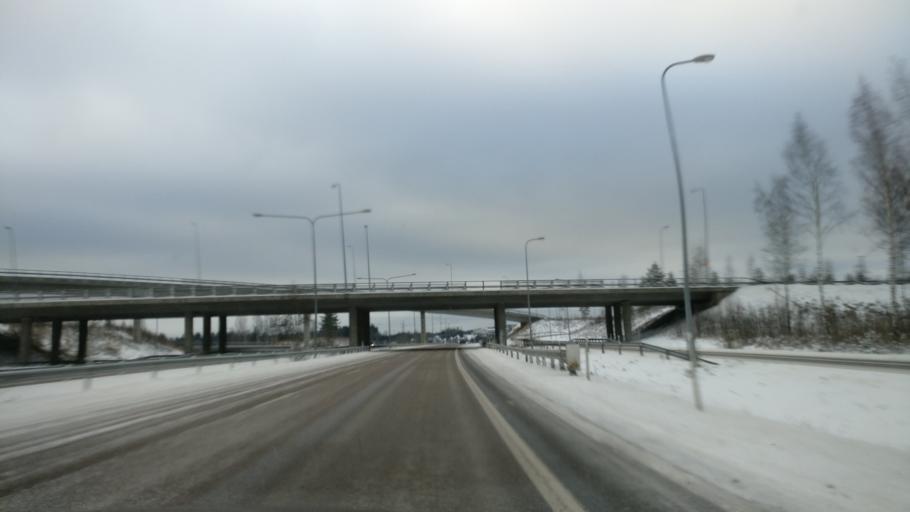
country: FI
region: Paijanne Tavastia
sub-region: Lahti
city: Lahti
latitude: 60.9715
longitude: 25.7221
